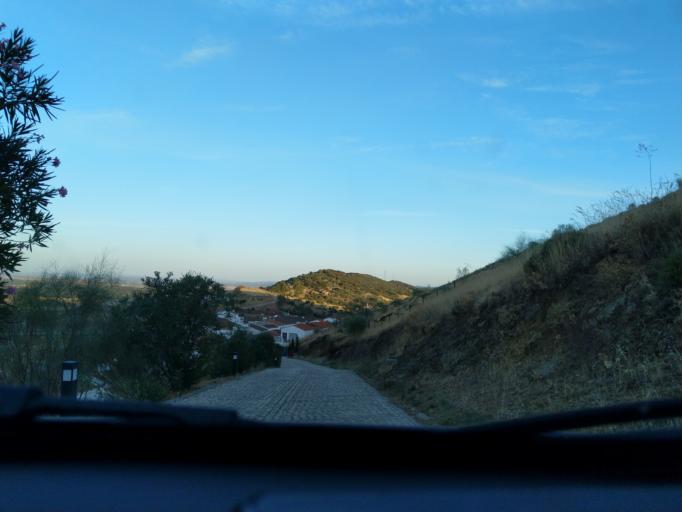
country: ES
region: Extremadura
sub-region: Provincia de Badajoz
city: Reina
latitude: 38.1870
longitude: -5.9512
